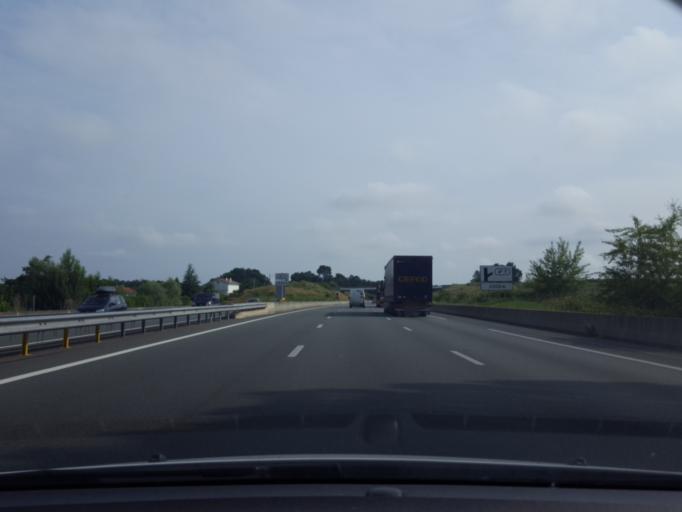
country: FR
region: Aquitaine
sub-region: Departement des Pyrenees-Atlantiques
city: Boucau
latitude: 43.5217
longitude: -1.4415
